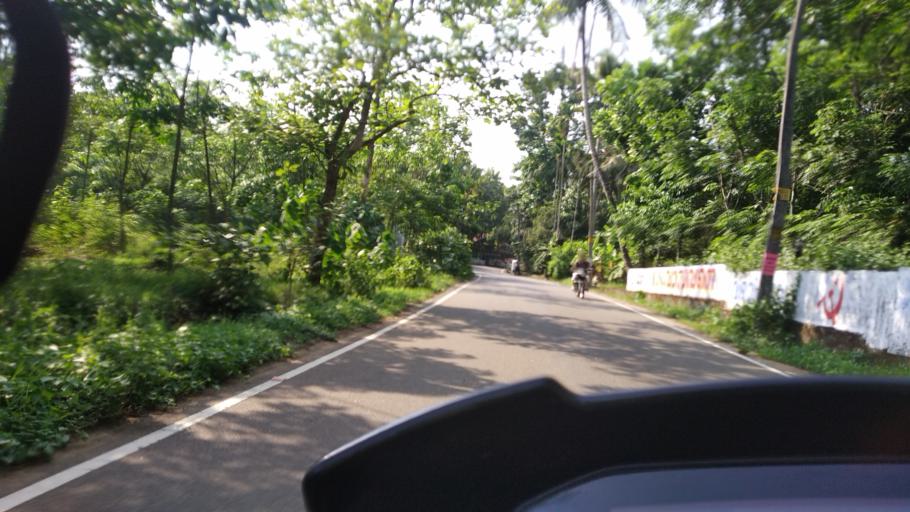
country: IN
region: Kerala
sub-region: Ernakulam
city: Piravam
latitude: 9.8347
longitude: 76.5404
